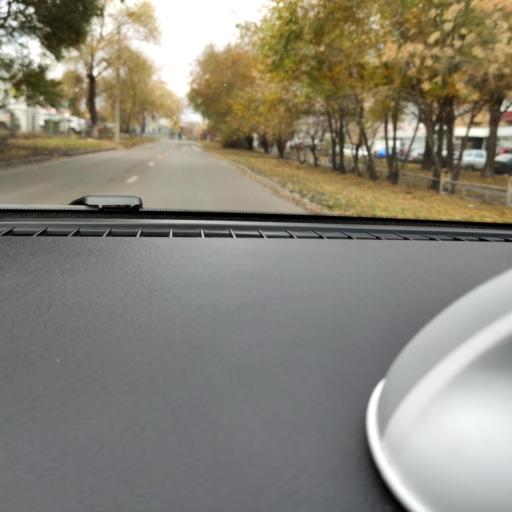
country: RU
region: Samara
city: Samara
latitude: 53.1961
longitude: 50.2000
